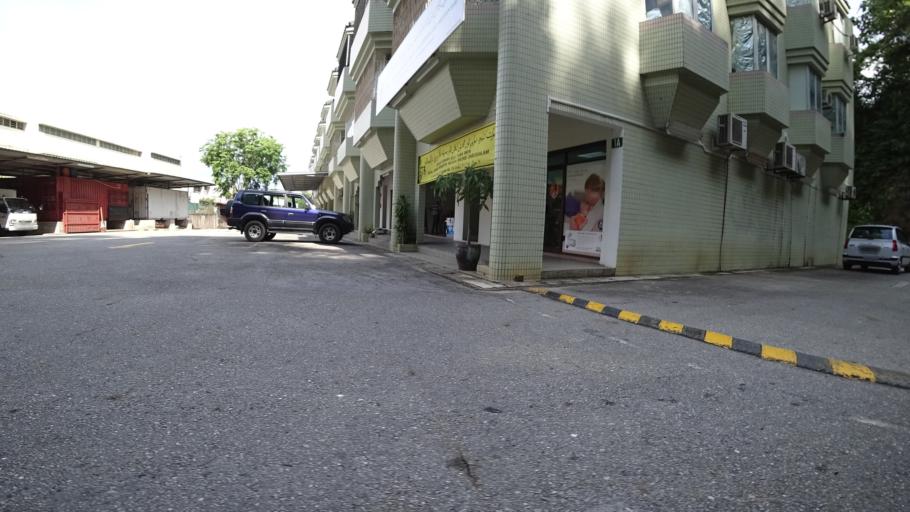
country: BN
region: Brunei and Muara
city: Bandar Seri Begawan
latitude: 4.8598
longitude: 114.8936
